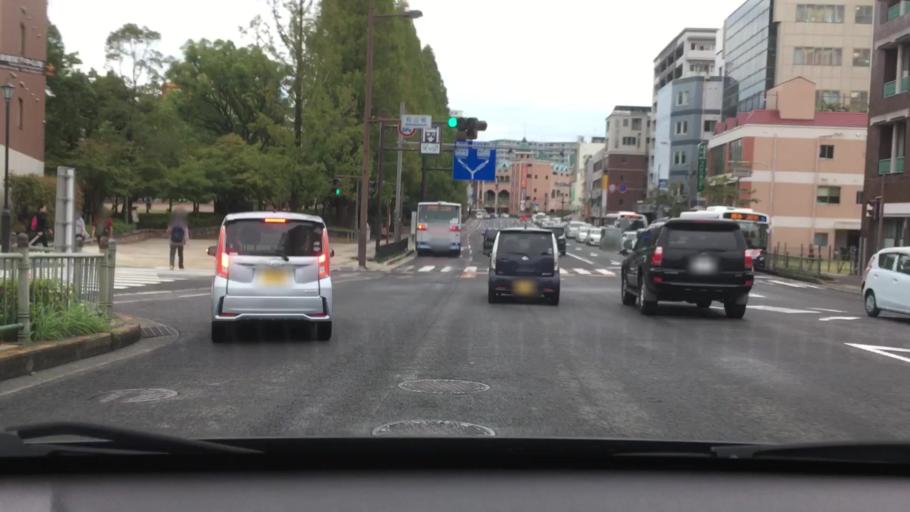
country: JP
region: Nagasaki
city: Nagasaki-shi
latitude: 32.7742
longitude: 129.8625
